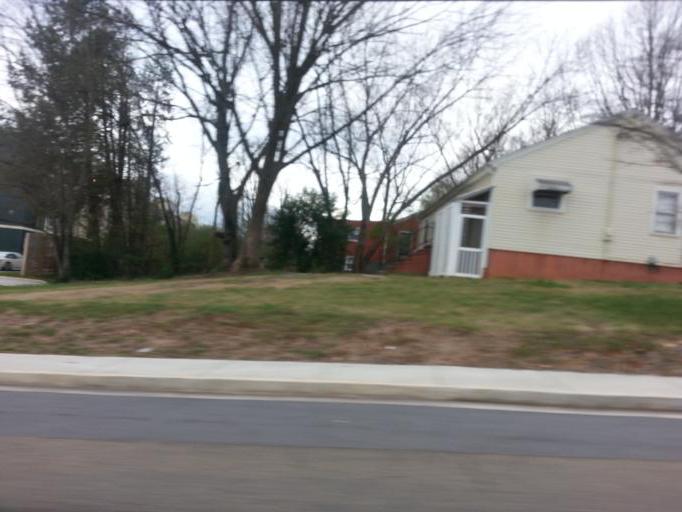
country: US
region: Tennessee
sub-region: Washington County
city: Johnson City
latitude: 36.3099
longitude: -82.3657
